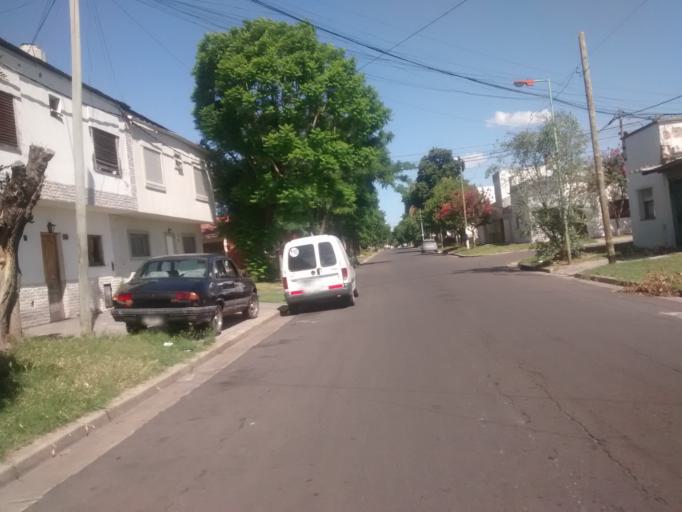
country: AR
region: Buenos Aires
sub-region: Partido de La Plata
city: La Plata
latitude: -34.9353
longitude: -57.9246
